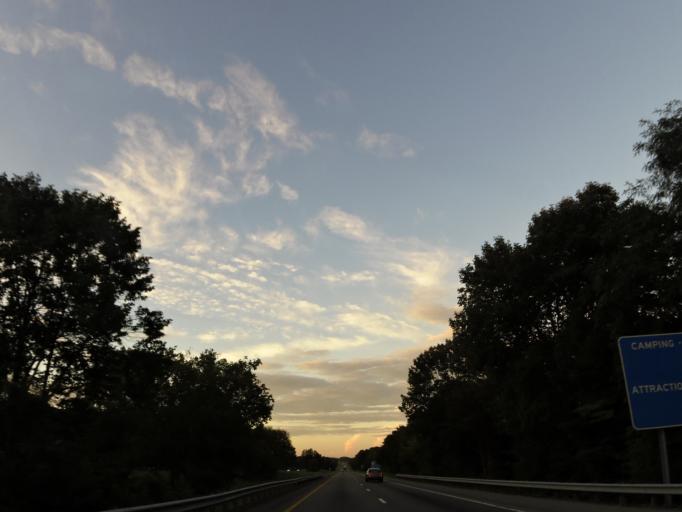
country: US
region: Tennessee
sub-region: McMinn County
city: Athens
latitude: 35.5304
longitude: -84.5840
